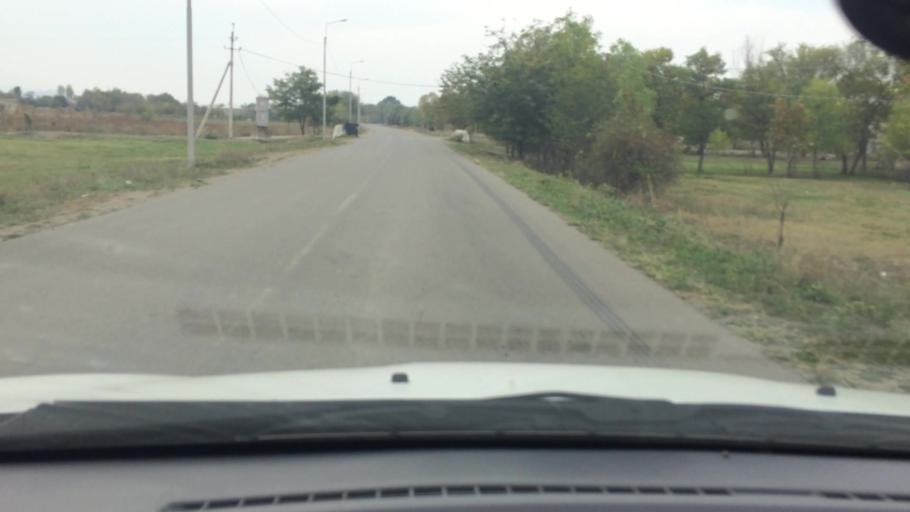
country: AM
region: Tavush
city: Berdavan
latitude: 41.3478
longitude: 44.9777
